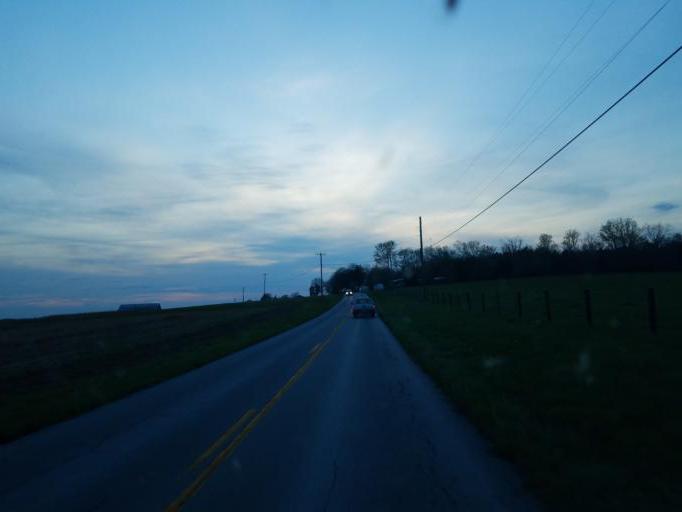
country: US
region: Kentucky
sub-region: Hart County
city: Munfordville
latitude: 37.2733
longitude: -85.8237
